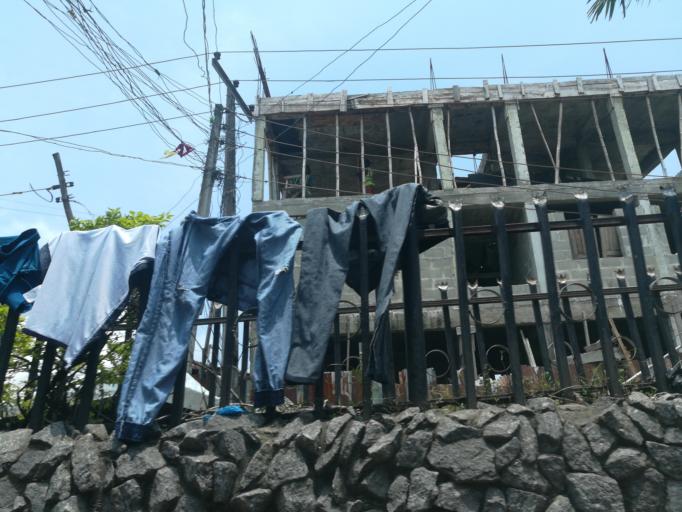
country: NG
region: Lagos
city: Lagos
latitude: 6.4549
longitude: 3.3984
